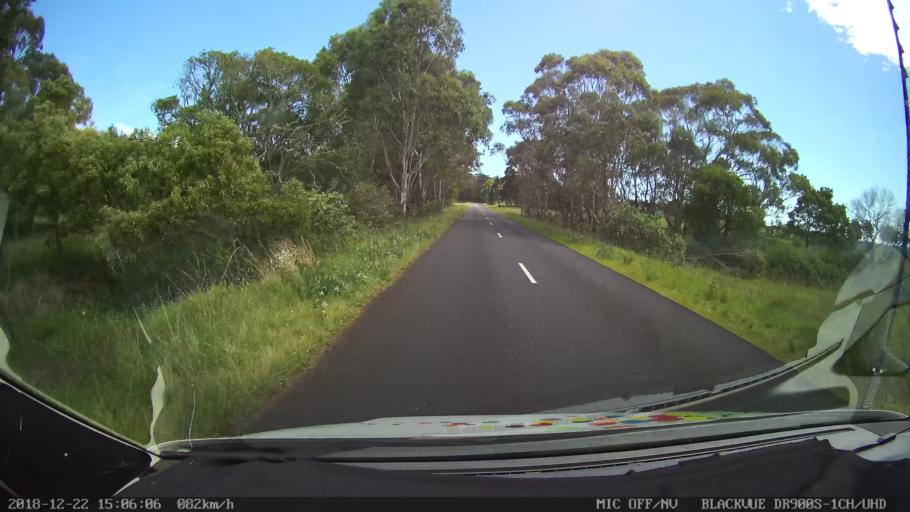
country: AU
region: New South Wales
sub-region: Bellingen
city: Dorrigo
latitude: -30.2903
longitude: 152.4304
